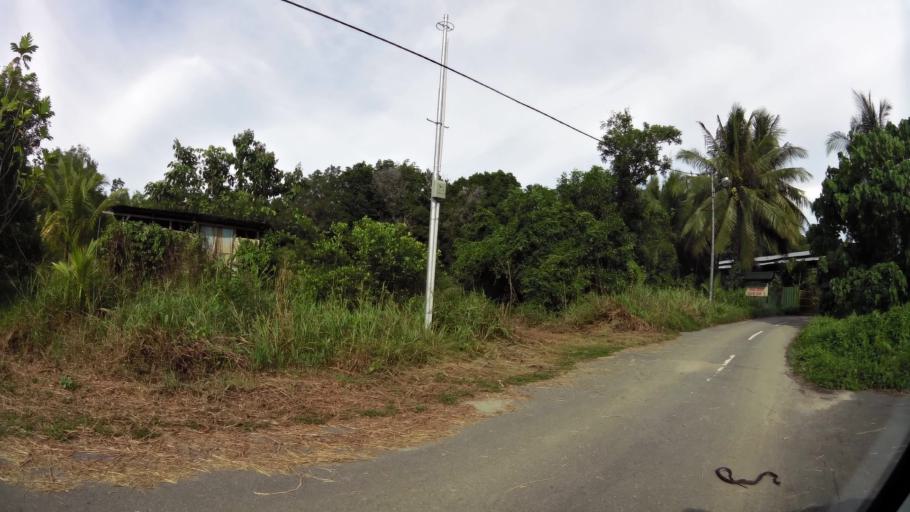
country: BN
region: Brunei and Muara
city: Bandar Seri Begawan
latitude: 4.9790
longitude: 115.0236
